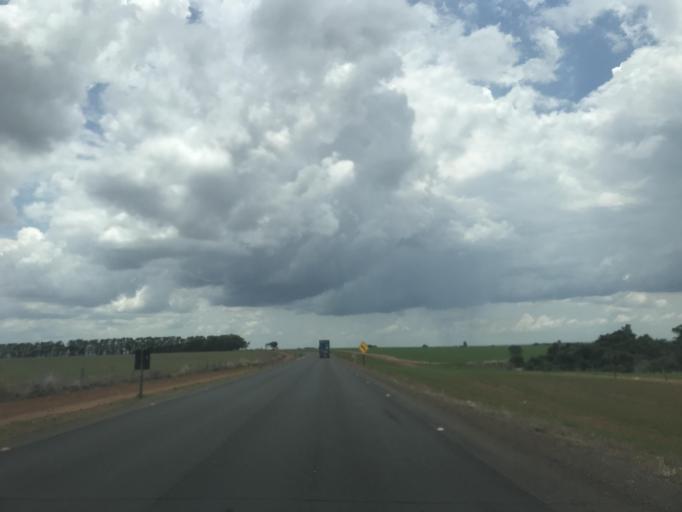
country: BR
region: Goias
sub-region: Vianopolis
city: Vianopolis
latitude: -16.7833
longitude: -48.5216
